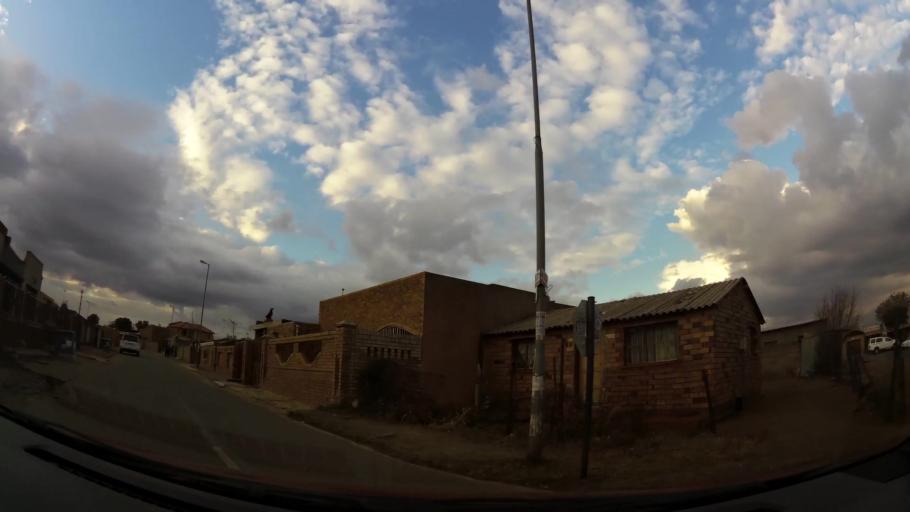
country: ZA
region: Gauteng
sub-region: City of Johannesburg Metropolitan Municipality
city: Soweto
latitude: -26.2467
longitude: 27.8310
